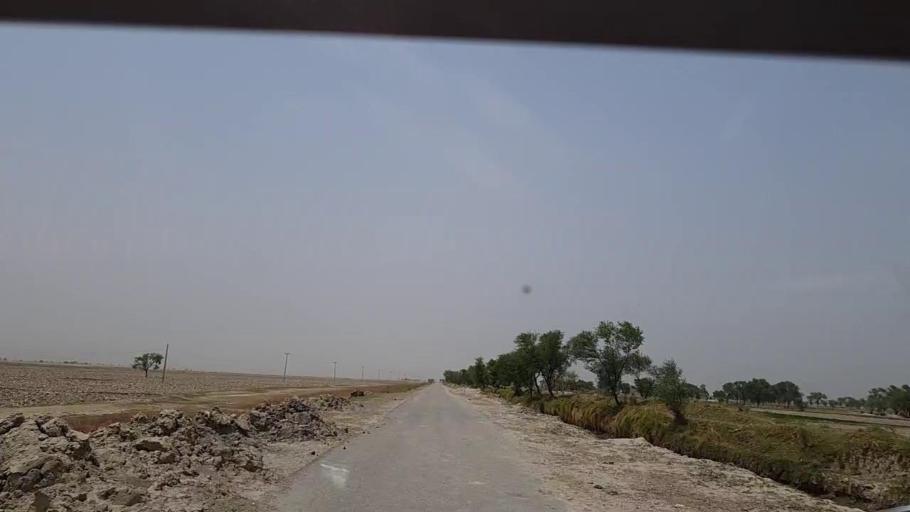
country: PK
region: Sindh
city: Khairpur Nathan Shah
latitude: 27.0260
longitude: 67.6207
